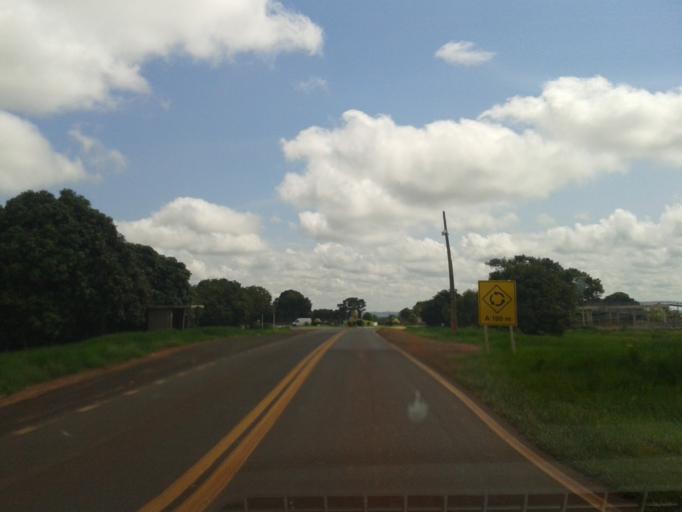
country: BR
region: Minas Gerais
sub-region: Centralina
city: Centralina
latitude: -18.7137
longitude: -49.1362
